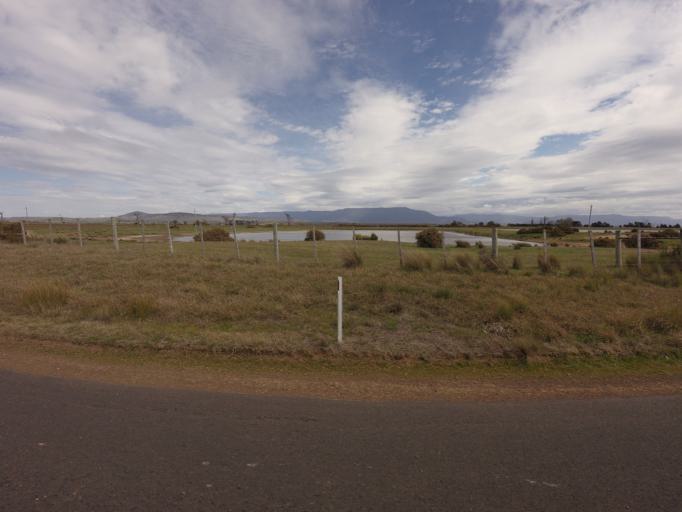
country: AU
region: Tasmania
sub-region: Northern Midlands
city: Evandale
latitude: -41.8293
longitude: 147.3254
